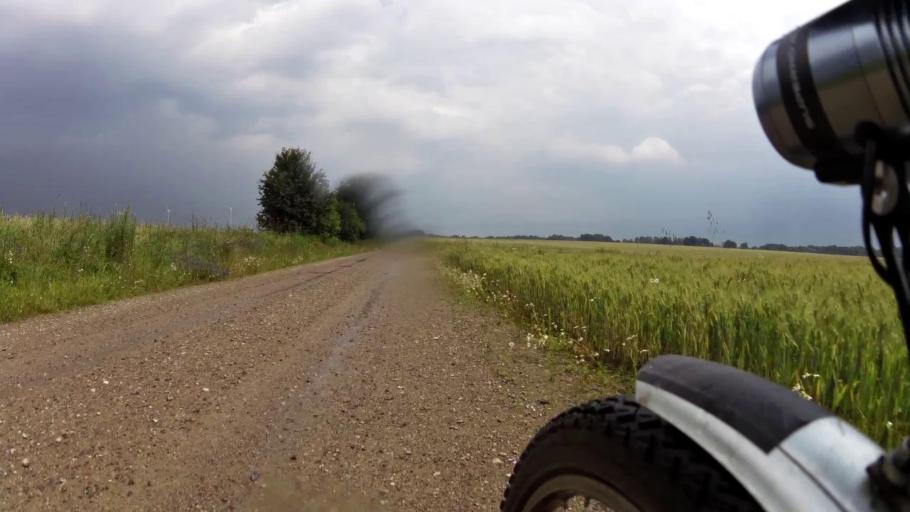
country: PL
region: West Pomeranian Voivodeship
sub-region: Powiat lobeski
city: Lobez
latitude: 53.7065
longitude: 15.6164
